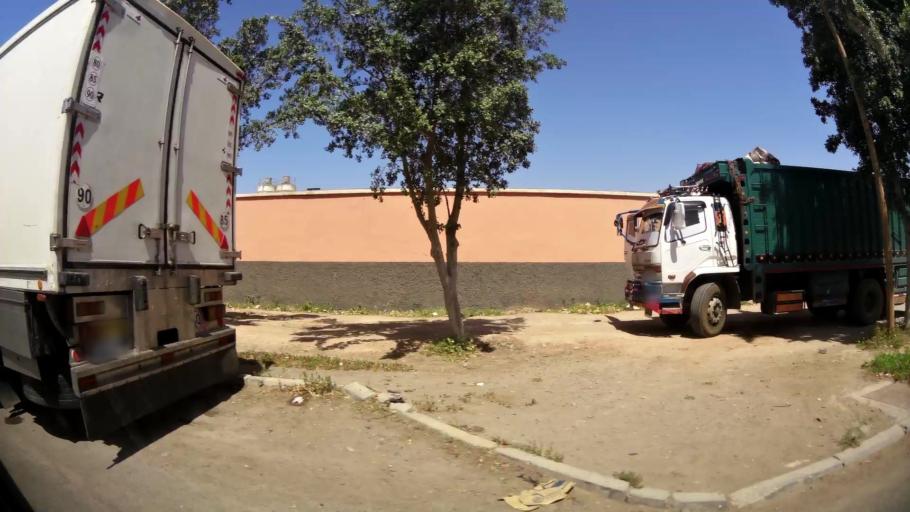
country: MA
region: Souss-Massa-Draa
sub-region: Inezgane-Ait Mellou
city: Inezgane
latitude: 30.3272
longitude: -9.4875
